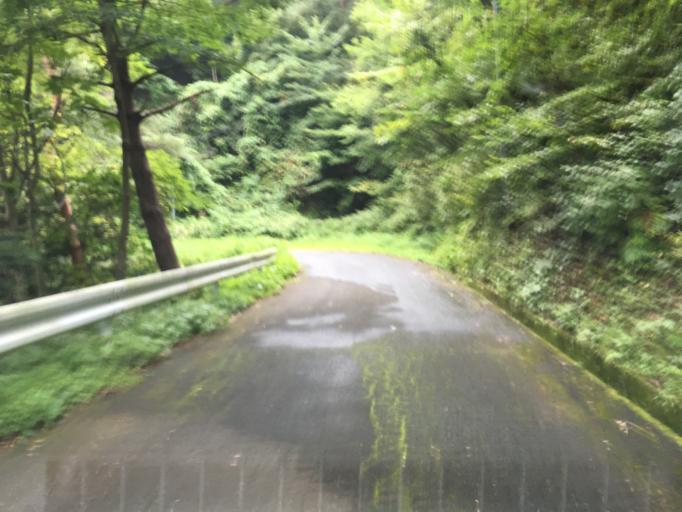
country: JP
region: Fukushima
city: Fukushima-shi
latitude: 37.8110
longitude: 140.3518
